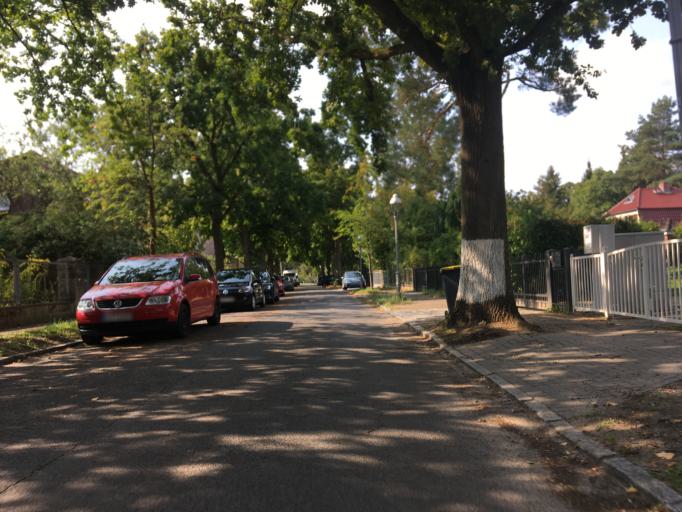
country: DE
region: Brandenburg
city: Glienicke
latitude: 52.6248
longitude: 13.3285
